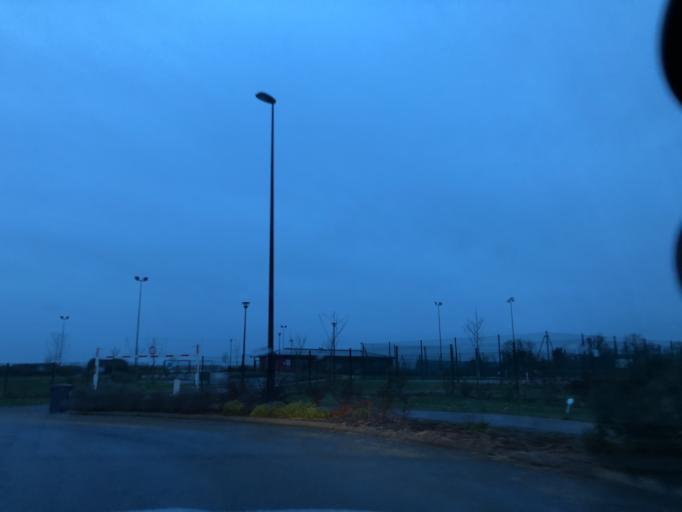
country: FR
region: Lower Normandy
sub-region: Departement du Calvados
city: Beuville
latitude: 49.2438
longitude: -0.3353
